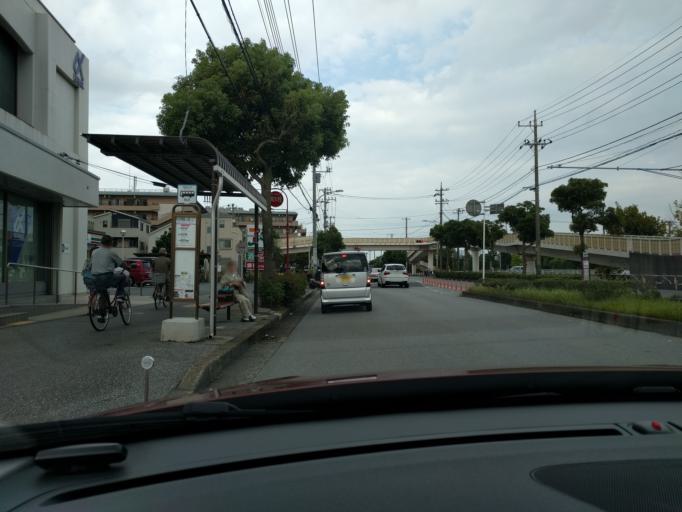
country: JP
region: Chiba
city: Funabashi
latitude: 35.6674
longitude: 140.0167
